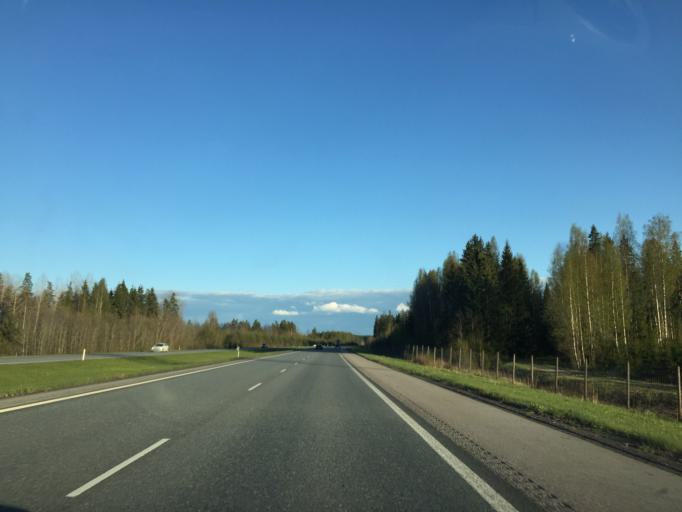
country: FI
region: Haeme
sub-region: Haemeenlinna
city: Tervakoski
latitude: 60.7831
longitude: 24.7050
